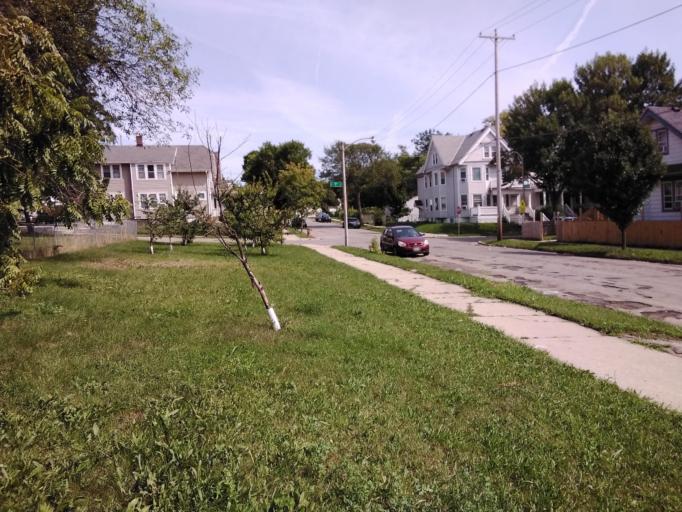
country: US
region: Wisconsin
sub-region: Milwaukee County
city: Shorewood
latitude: 43.0790
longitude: -87.9230
